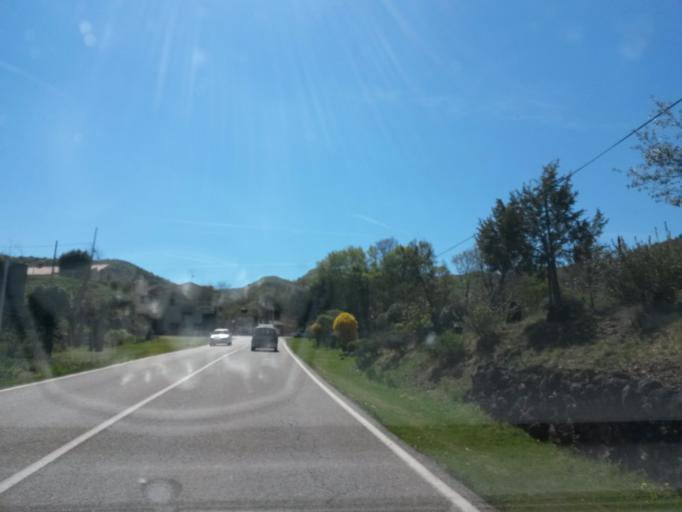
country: ES
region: Catalonia
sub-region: Provincia de Girona
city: Sant Cristofol de les Fonts
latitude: 42.1493
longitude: 2.5299
